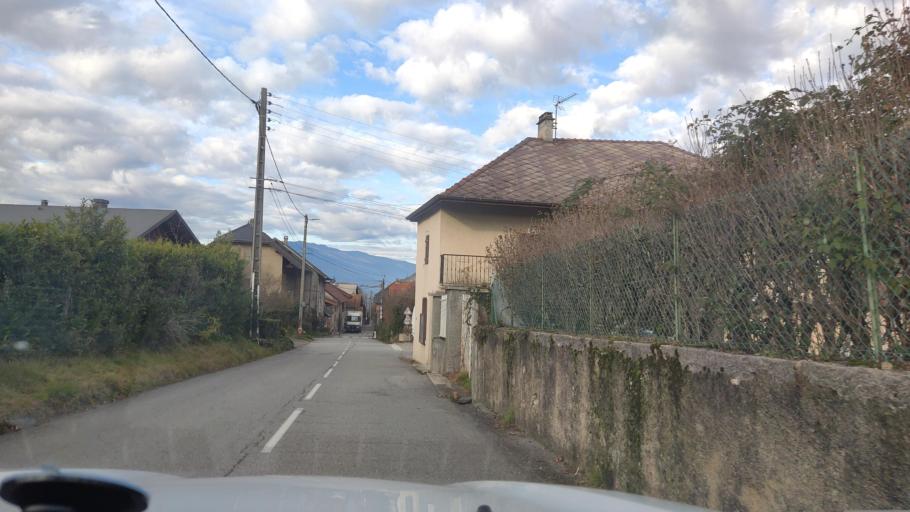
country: FR
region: Rhone-Alpes
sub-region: Departement de la Savoie
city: Brison-Saint-Innocent
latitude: 45.7291
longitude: 5.8865
